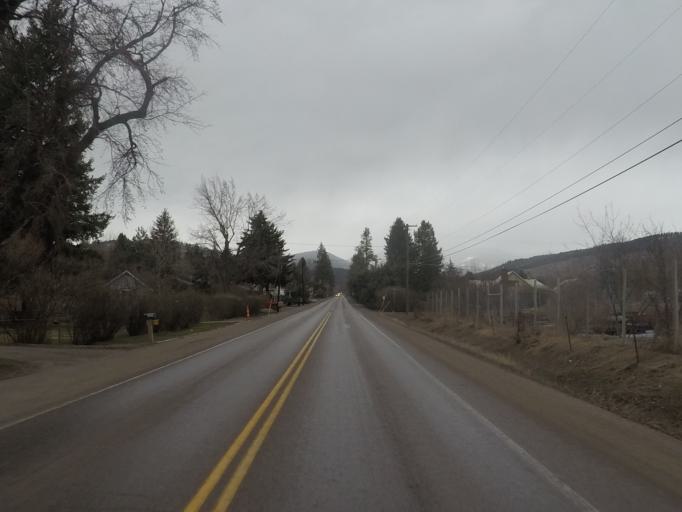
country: US
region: Montana
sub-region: Missoula County
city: East Missoula
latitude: 46.8854
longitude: -113.9657
